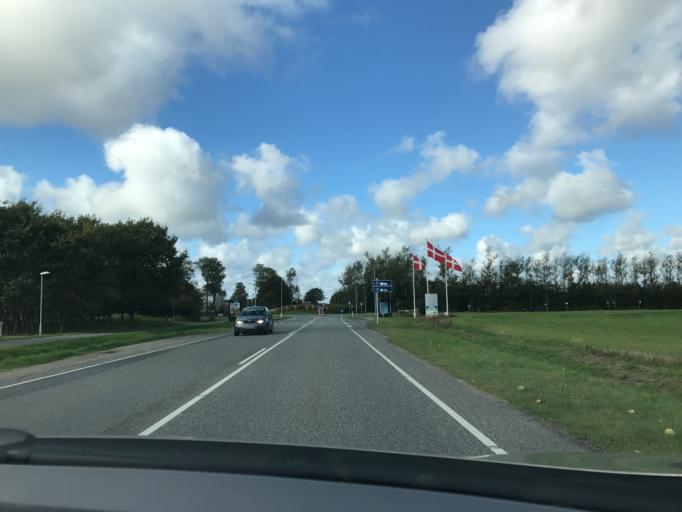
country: DK
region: South Denmark
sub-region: Billund Kommune
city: Billund
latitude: 55.7250
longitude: 9.1340
